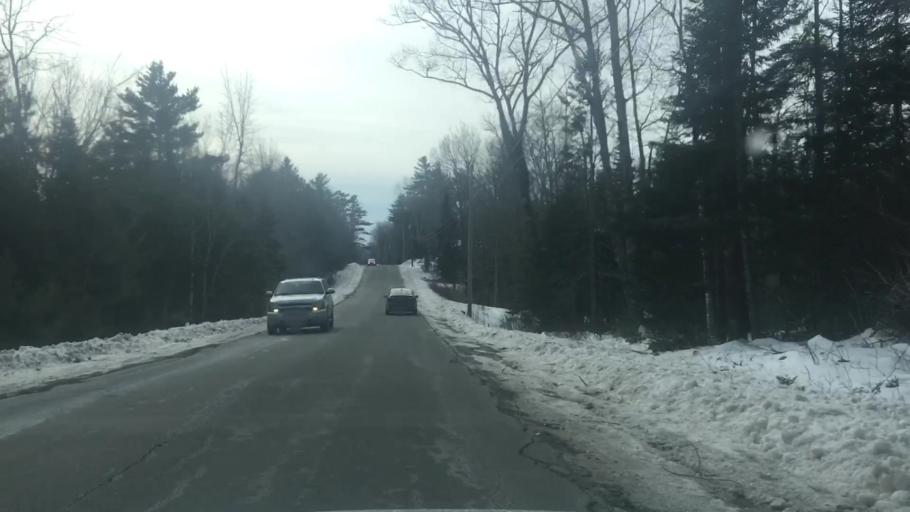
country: US
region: Maine
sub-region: Hancock County
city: Orland
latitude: 44.6042
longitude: -68.7187
